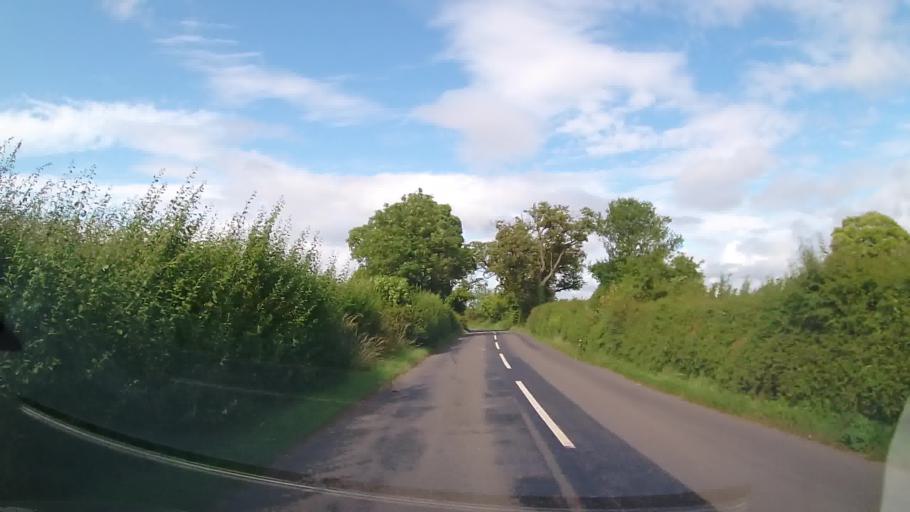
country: GB
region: England
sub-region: Shropshire
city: Petton
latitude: 52.8216
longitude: -2.8162
